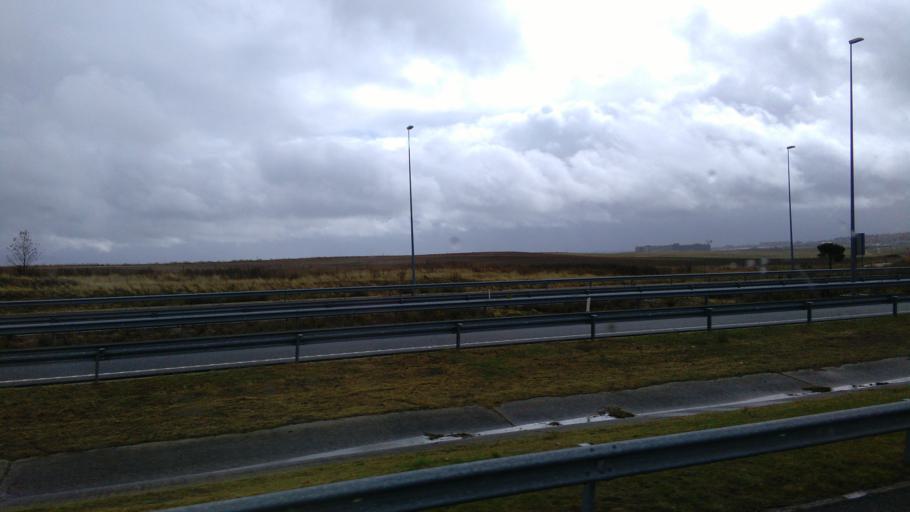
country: ES
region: Madrid
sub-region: Provincia de Madrid
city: Alcorcon
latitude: 40.3256
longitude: -3.8171
